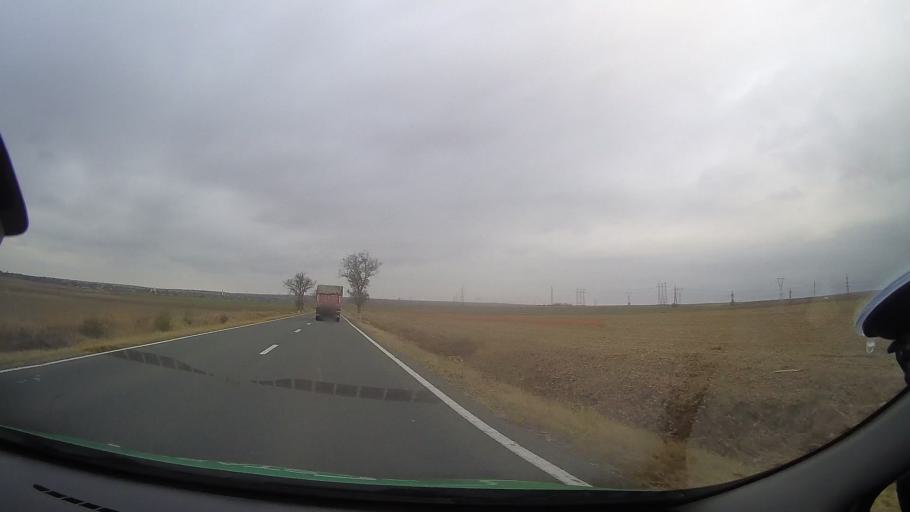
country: RO
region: Constanta
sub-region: Comuna Castelu
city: Castelu
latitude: 44.2523
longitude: 28.3547
